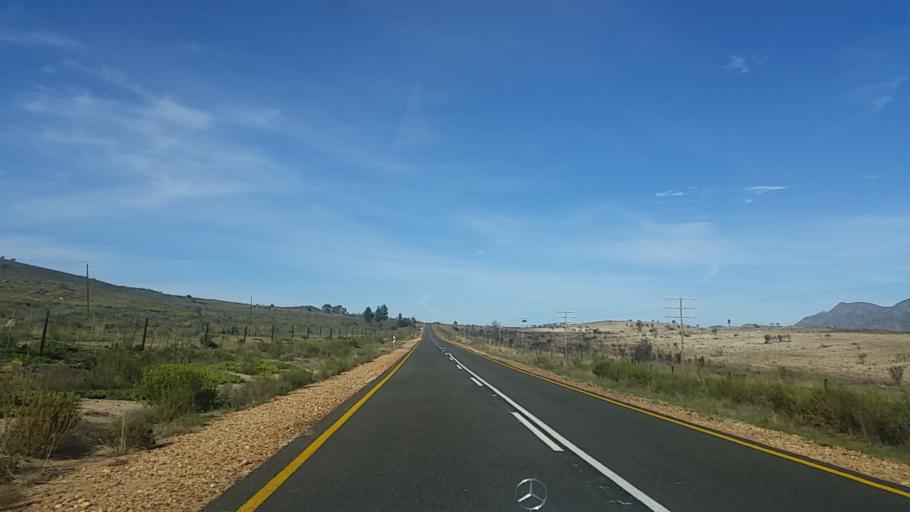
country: ZA
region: Western Cape
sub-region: Eden District Municipality
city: George
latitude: -33.7845
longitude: 22.6648
